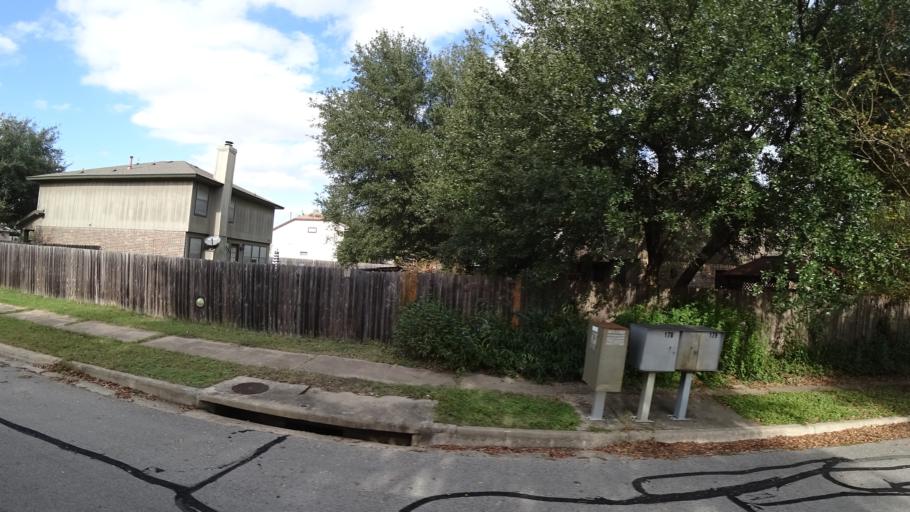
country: US
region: Texas
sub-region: Travis County
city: Pflugerville
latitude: 30.4363
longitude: -97.6269
